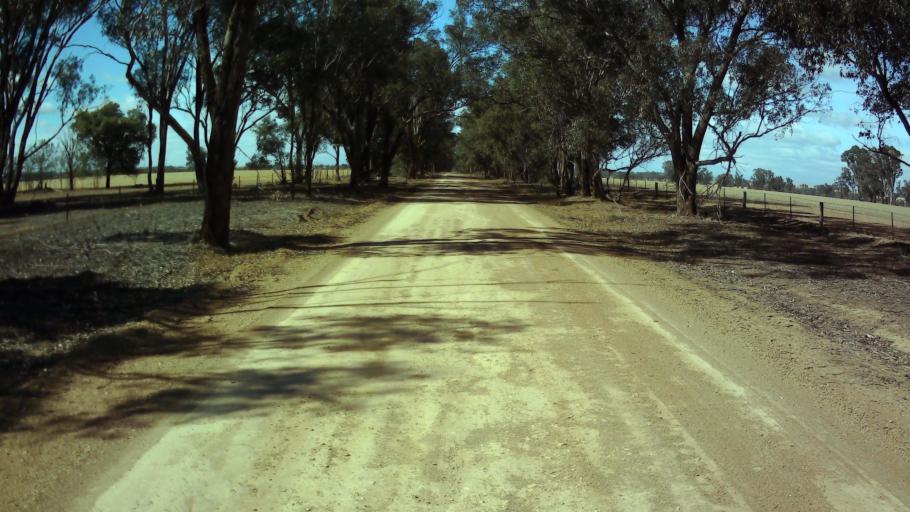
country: AU
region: New South Wales
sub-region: Weddin
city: Grenfell
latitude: -34.0462
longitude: 148.3147
